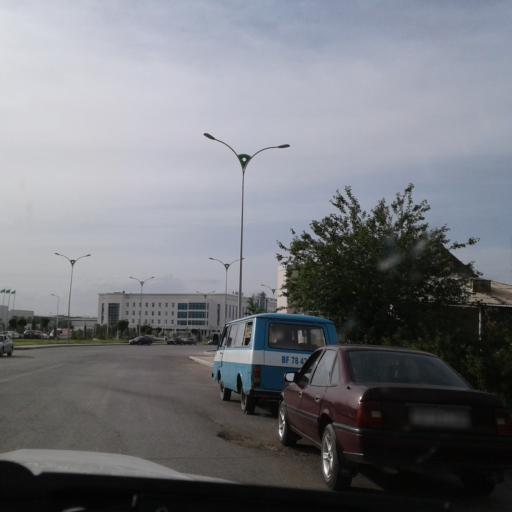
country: TM
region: Mary
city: Mary
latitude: 37.5806
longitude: 61.8717
